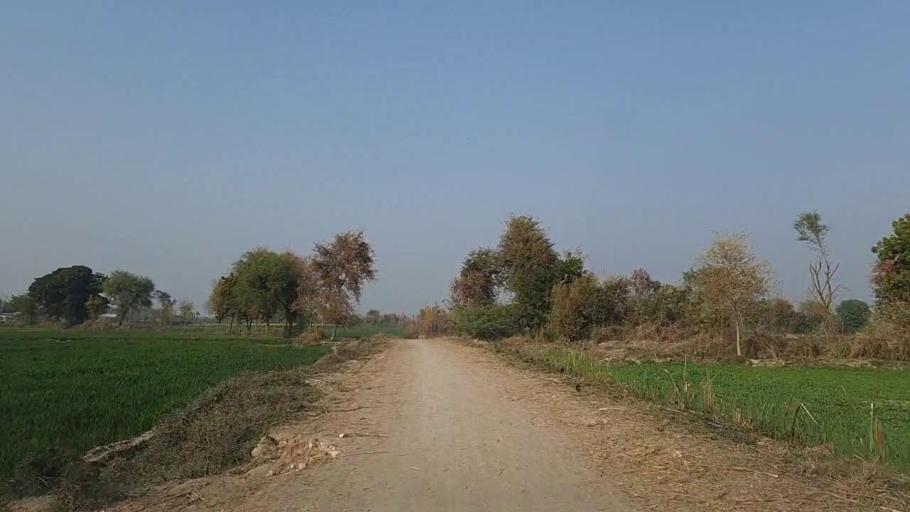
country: PK
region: Sindh
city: Nawabshah
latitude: 26.3540
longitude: 68.4741
